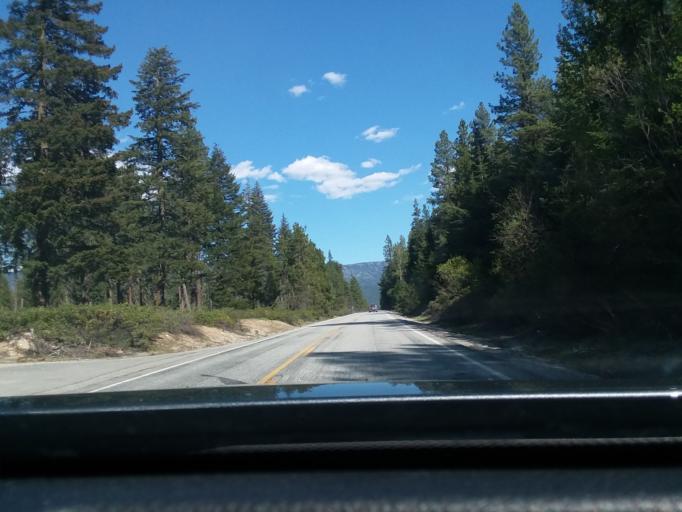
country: US
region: Washington
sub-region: Chelan County
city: Leavenworth
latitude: 47.8035
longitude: -120.6943
